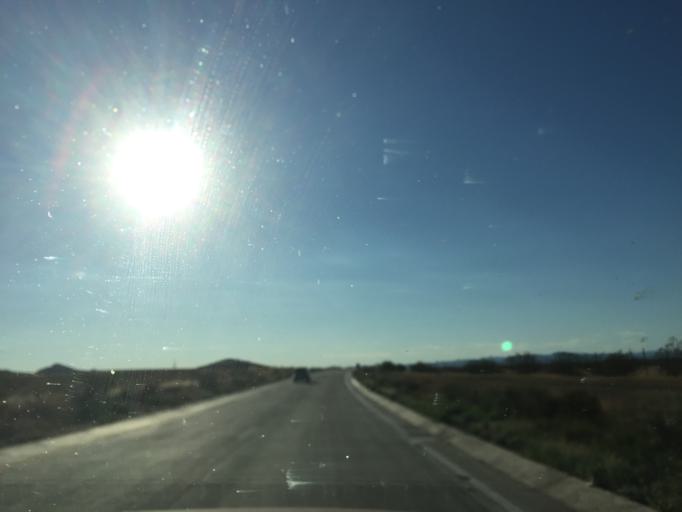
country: US
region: Arizona
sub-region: Maricopa County
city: Anthem
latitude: 33.7704
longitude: -112.1696
